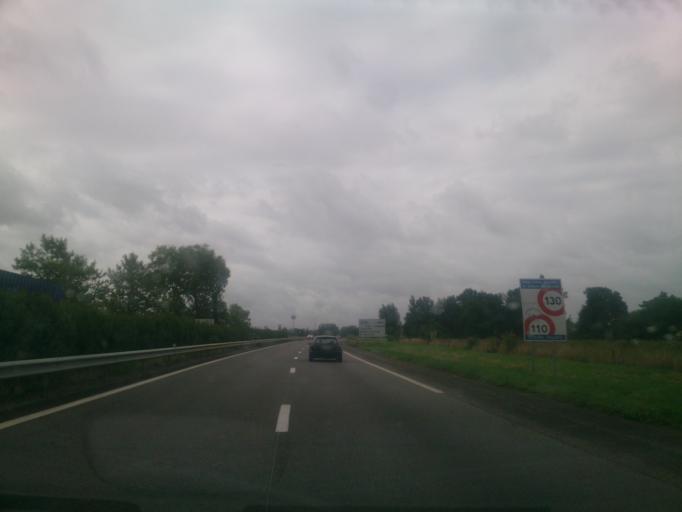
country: FR
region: Midi-Pyrenees
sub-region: Departement de la Haute-Garonne
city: Noe
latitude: 43.3484
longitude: 1.2652
